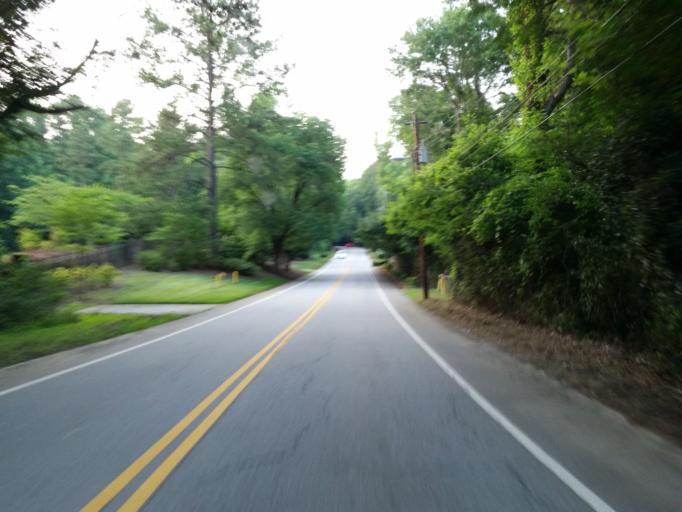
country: US
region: Georgia
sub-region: Cobb County
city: Vinings
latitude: 33.8862
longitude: -84.4266
